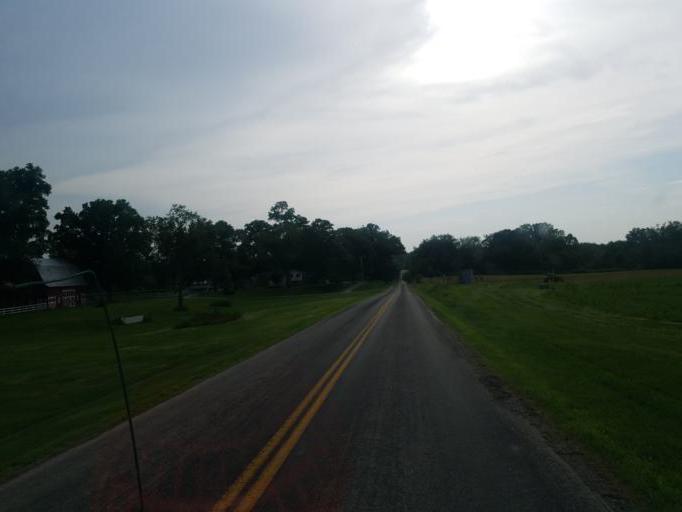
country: US
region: Ohio
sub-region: Wayne County
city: West Salem
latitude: 40.9009
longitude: -82.1486
